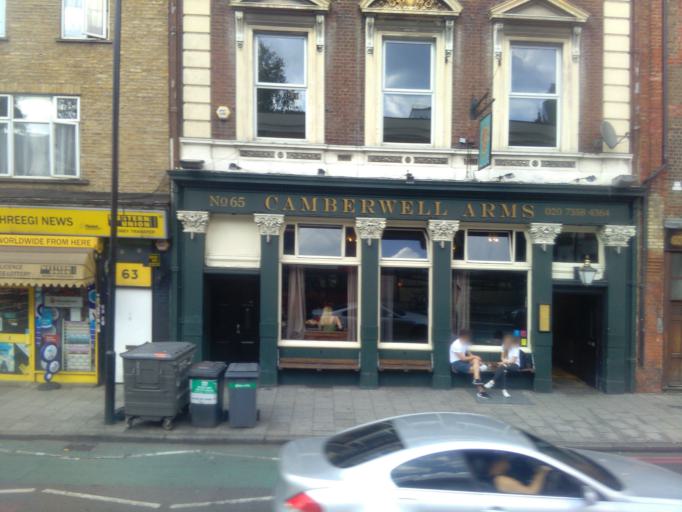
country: GB
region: England
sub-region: Greater London
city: Camberwell
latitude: 51.4737
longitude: -0.0883
